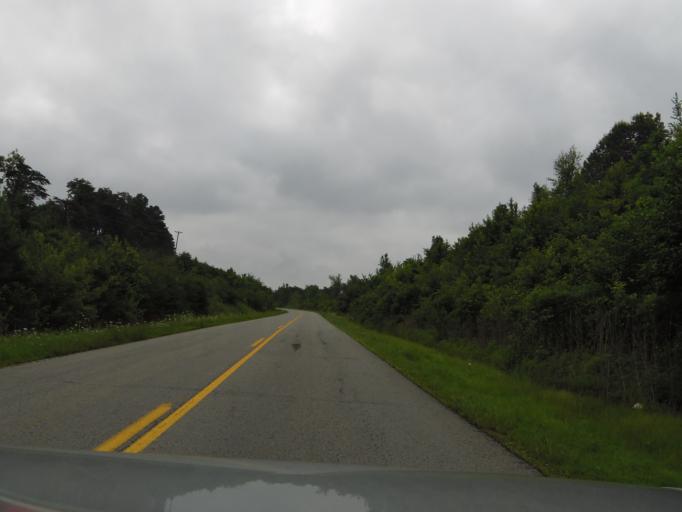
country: US
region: Kentucky
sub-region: Muhlenberg County
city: Morehead
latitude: 37.2745
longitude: -87.2948
